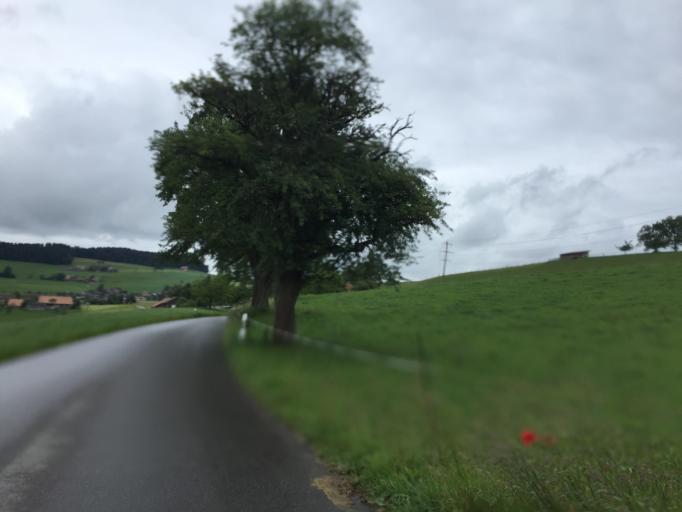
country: CH
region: Bern
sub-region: Bern-Mittelland District
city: Biglen
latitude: 46.9073
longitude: 7.6224
